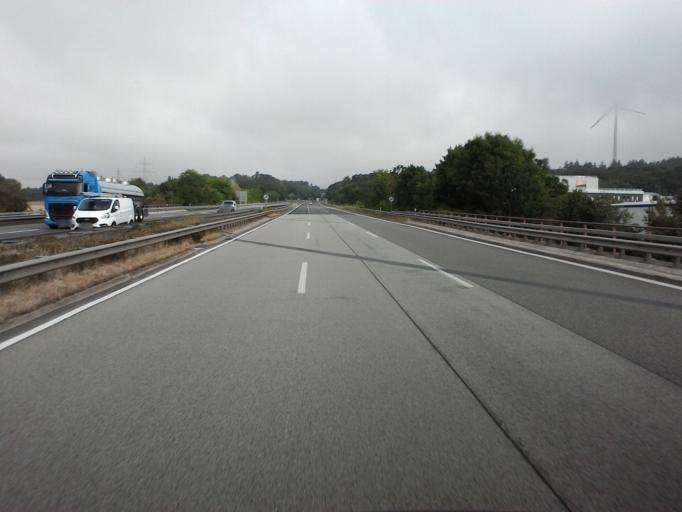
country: DE
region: Rheinland-Pfalz
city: Wiebelsheim
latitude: 50.0769
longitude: 7.6211
